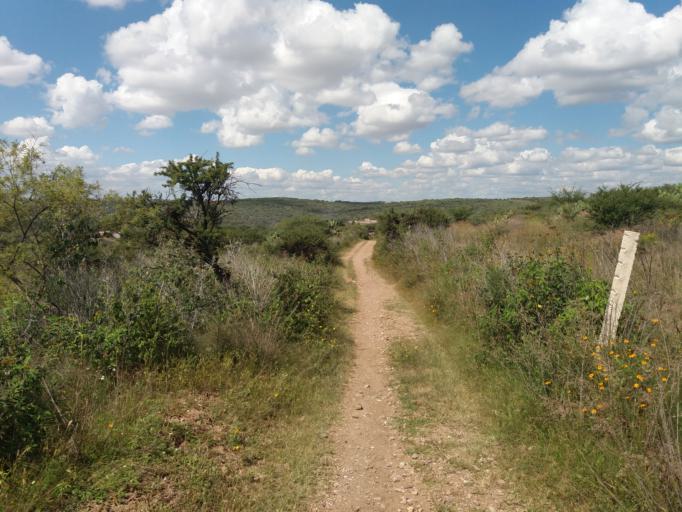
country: MX
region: Aguascalientes
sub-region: Aguascalientes
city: San Sebastian [Fraccionamiento]
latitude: 21.8025
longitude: -102.2425
